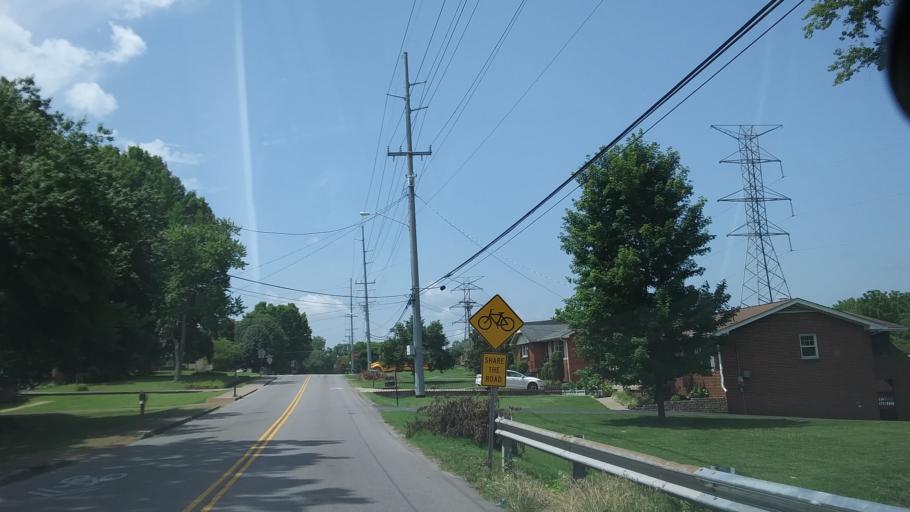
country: US
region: Tennessee
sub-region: Davidson County
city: Belle Meade
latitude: 36.1506
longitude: -86.8844
